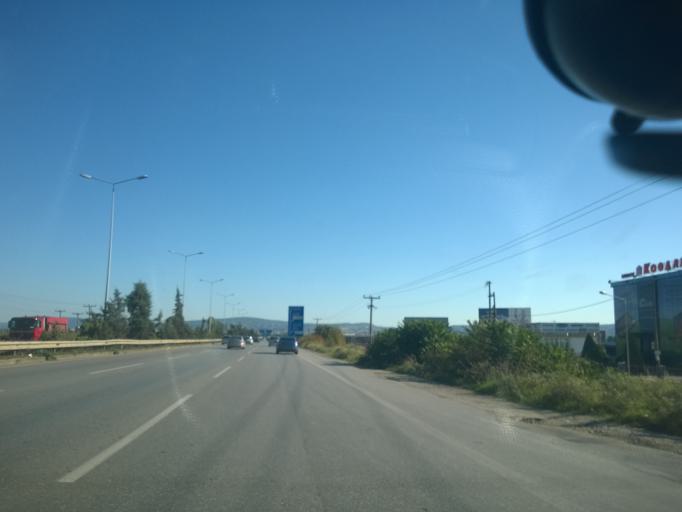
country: GR
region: Central Macedonia
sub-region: Nomos Thessalonikis
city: Thermi
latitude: 40.5469
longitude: 23.0036
